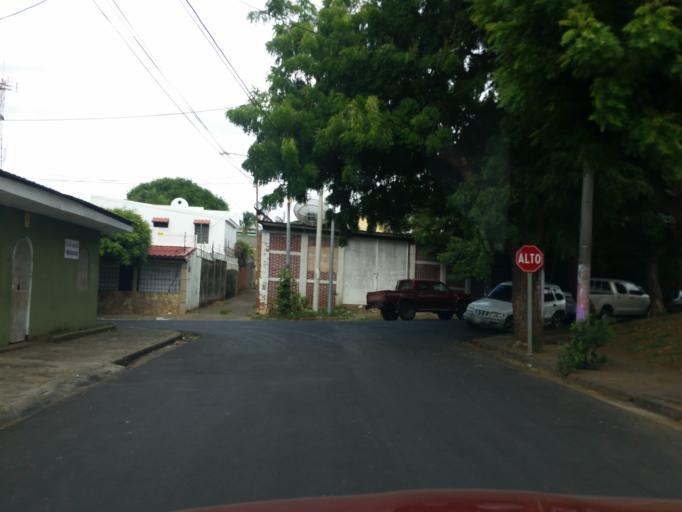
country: NI
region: Managua
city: Managua
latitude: 12.1426
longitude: -86.2787
